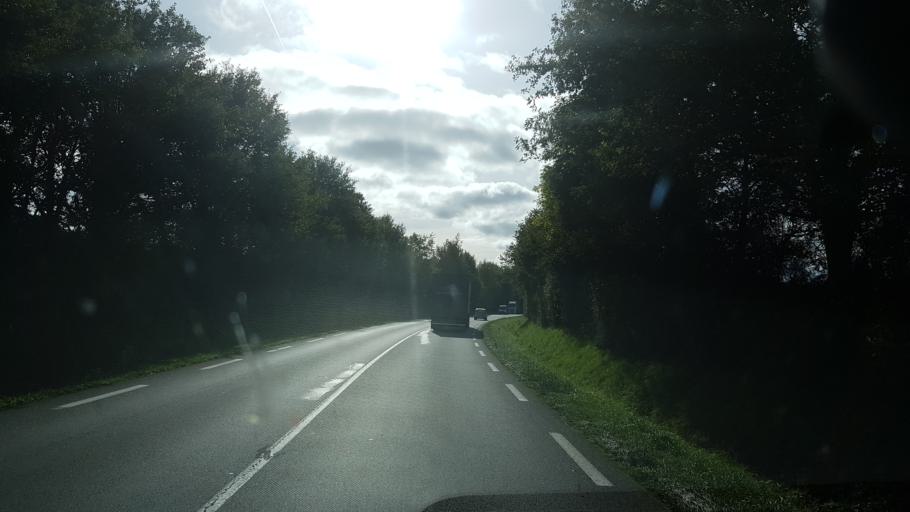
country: FR
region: Poitou-Charentes
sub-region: Departement de la Charente
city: Confolens
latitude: 46.0474
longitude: 0.6666
